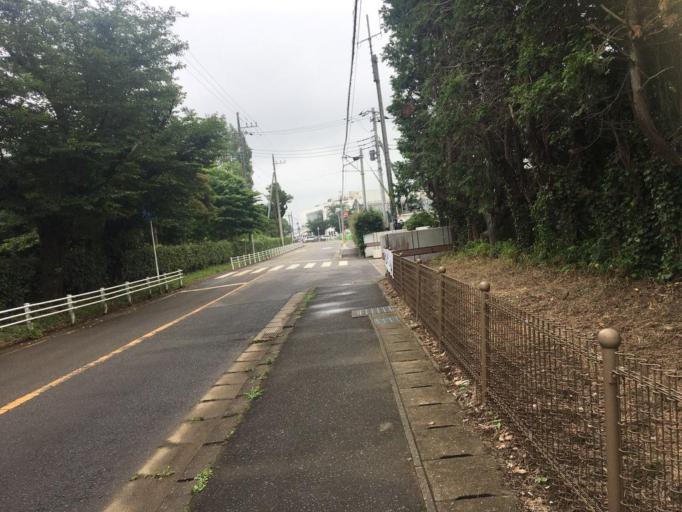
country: JP
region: Chiba
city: Sakura
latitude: 35.7197
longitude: 140.2220
